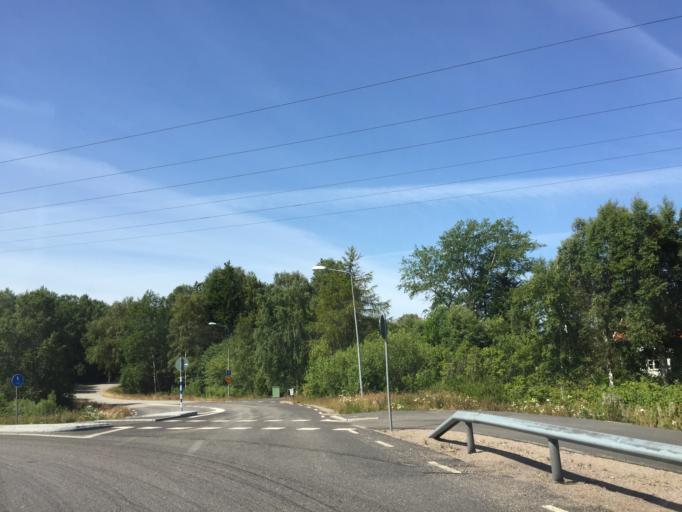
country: SE
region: Vaestra Goetaland
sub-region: Lysekils Kommun
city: Lysekil
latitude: 58.3037
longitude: 11.4761
